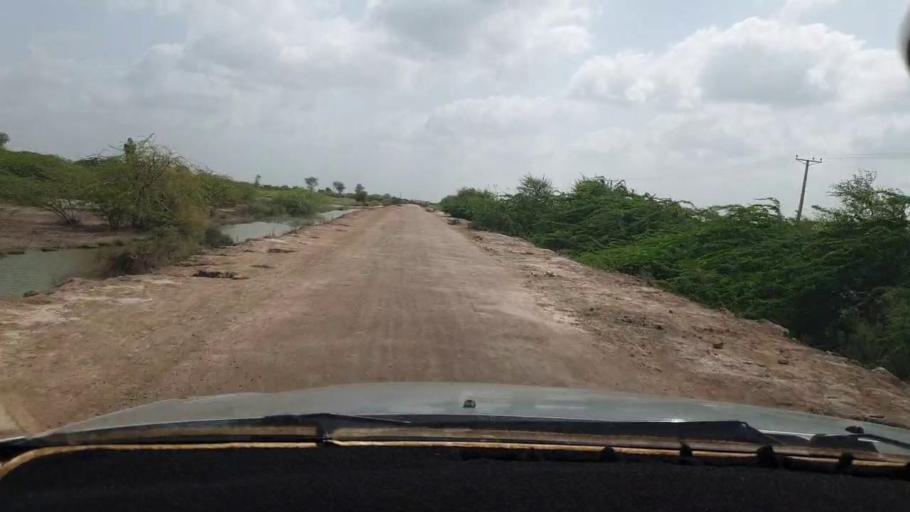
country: PK
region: Sindh
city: Tando Bago
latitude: 24.7208
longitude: 69.1373
